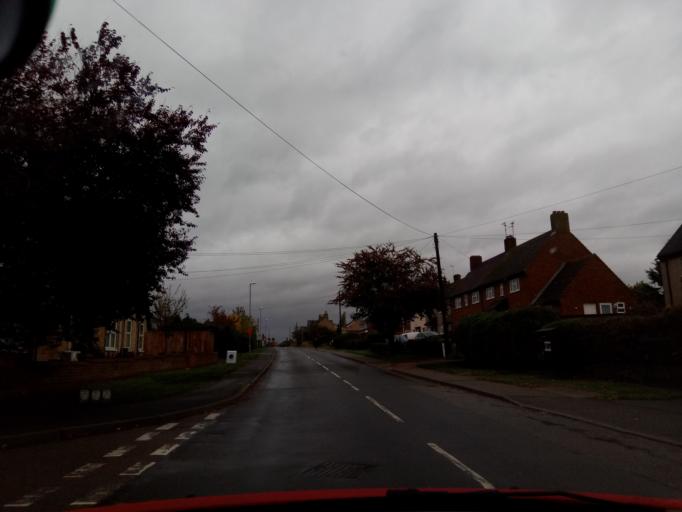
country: GB
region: England
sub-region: Cambridgeshire
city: Sawtry
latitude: 52.4347
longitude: -0.2813
